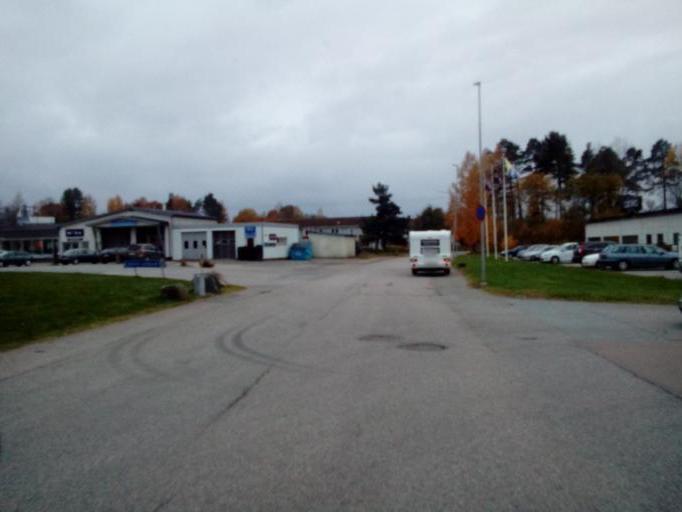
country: SE
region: OErebro
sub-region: Laxa Kommun
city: Laxa
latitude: 58.9859
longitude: 14.6350
